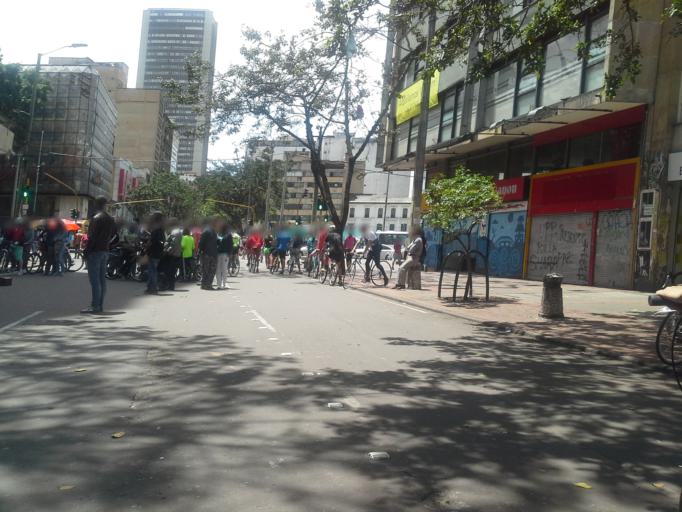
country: CO
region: Bogota D.C.
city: Bogota
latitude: 4.6058
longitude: -74.0715
